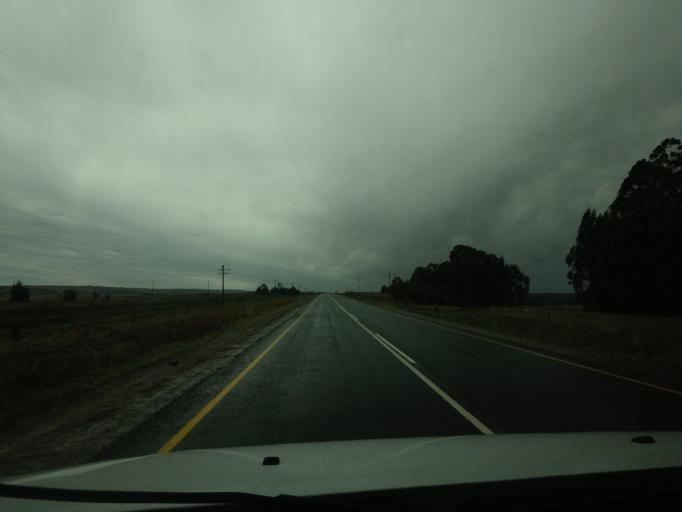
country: ZA
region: Mpumalanga
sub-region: Nkangala District Municipality
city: Belfast
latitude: -25.4806
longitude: 30.0937
